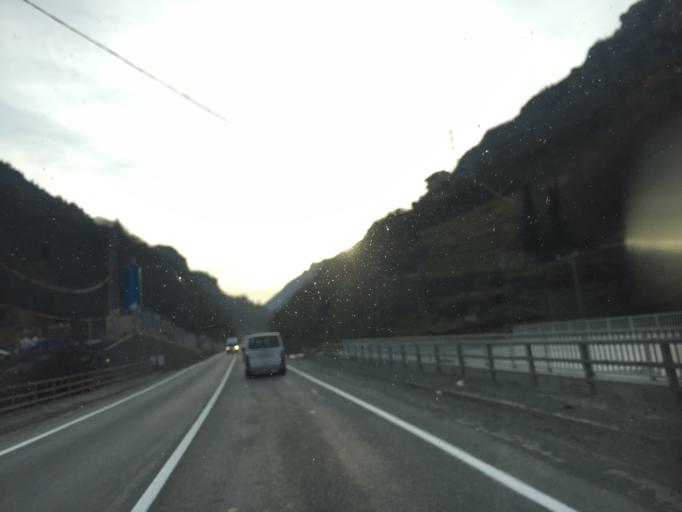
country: TR
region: Trabzon
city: Macka
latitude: 40.7435
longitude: 39.5553
